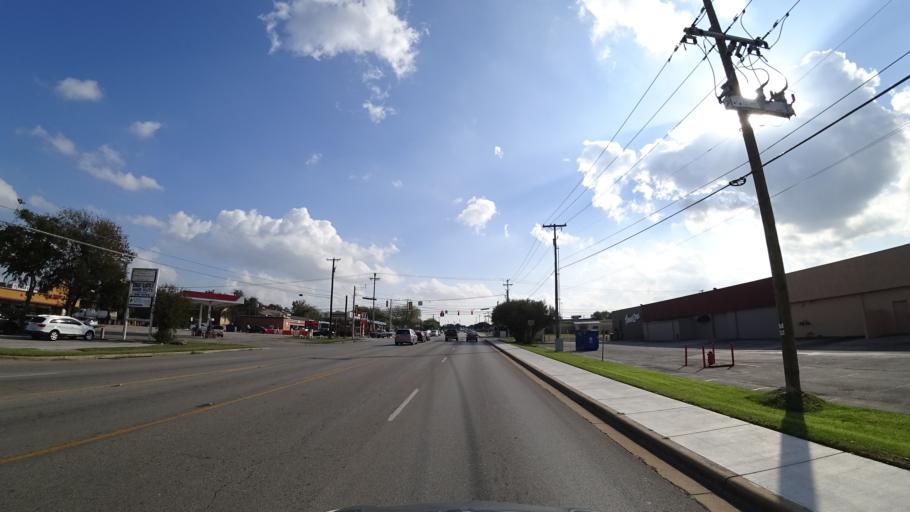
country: US
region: Texas
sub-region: Williamson County
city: Round Rock
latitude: 30.4943
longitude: -97.6758
